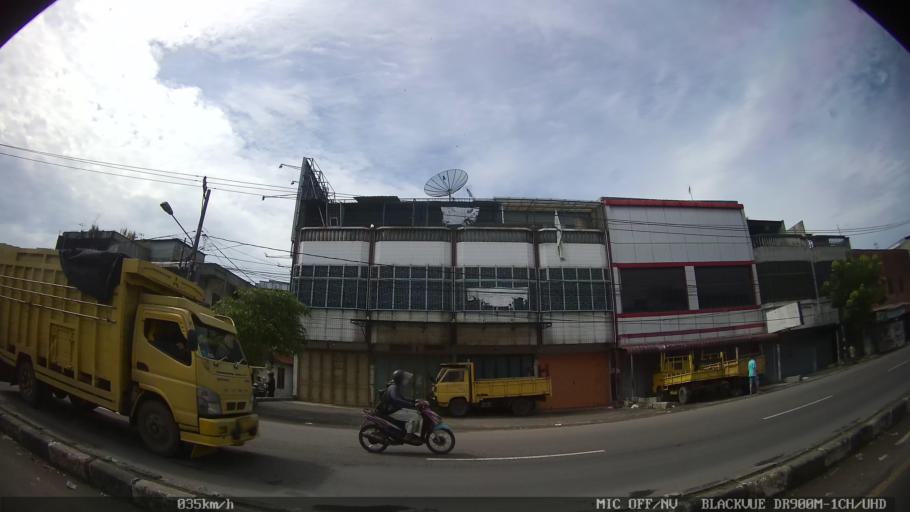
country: ID
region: North Sumatra
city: Medan
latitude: 3.6260
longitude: 98.6659
